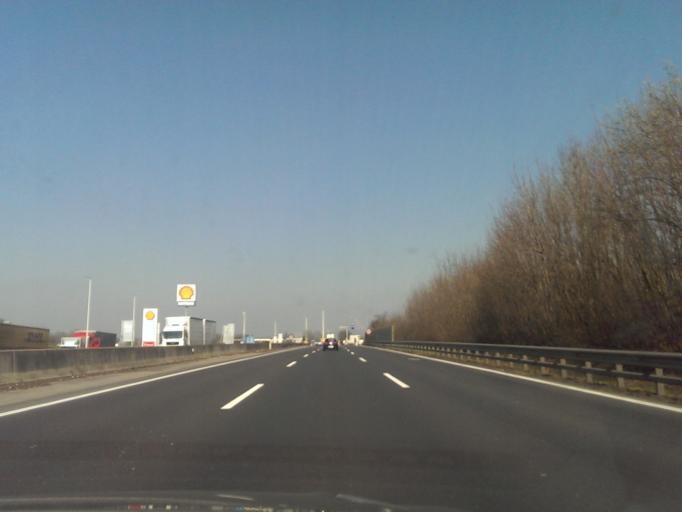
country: AT
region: Upper Austria
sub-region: Politischer Bezirk Scharding
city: Sankt Marienkirchen bei Schaerding
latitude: 48.3999
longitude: 13.4266
